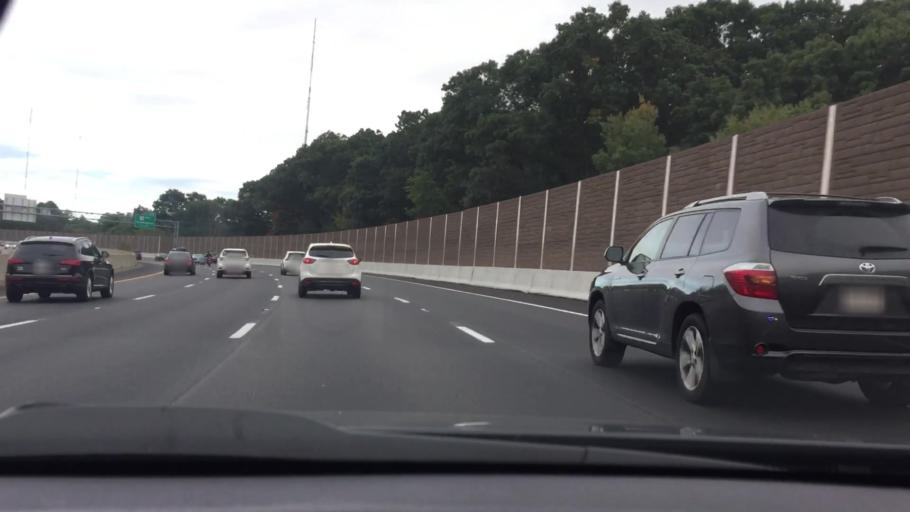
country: US
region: Massachusetts
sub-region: Norfolk County
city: Needham
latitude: 42.3215
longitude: -71.2483
